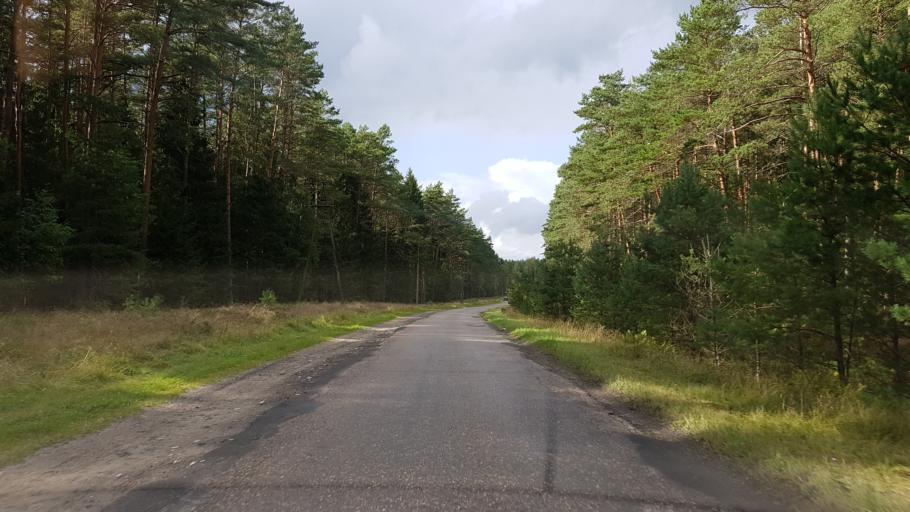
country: PL
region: West Pomeranian Voivodeship
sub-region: Powiat bialogardzki
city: Tychowo
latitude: 54.0443
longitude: 16.3169
